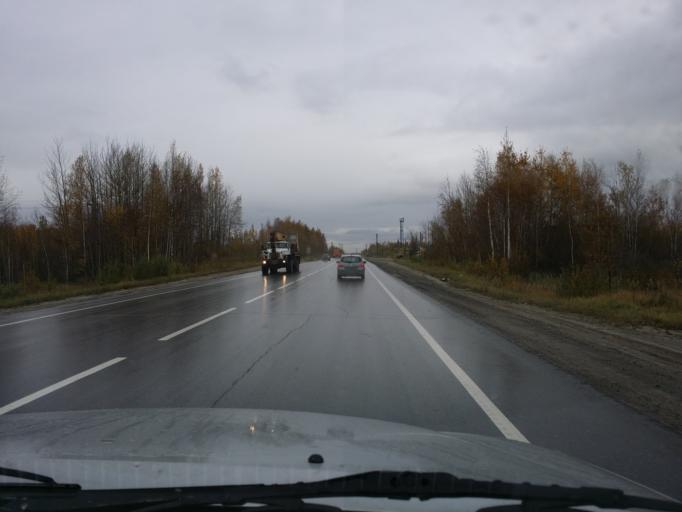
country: RU
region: Khanty-Mansiyskiy Avtonomnyy Okrug
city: Megion
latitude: 61.0701
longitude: 76.1162
